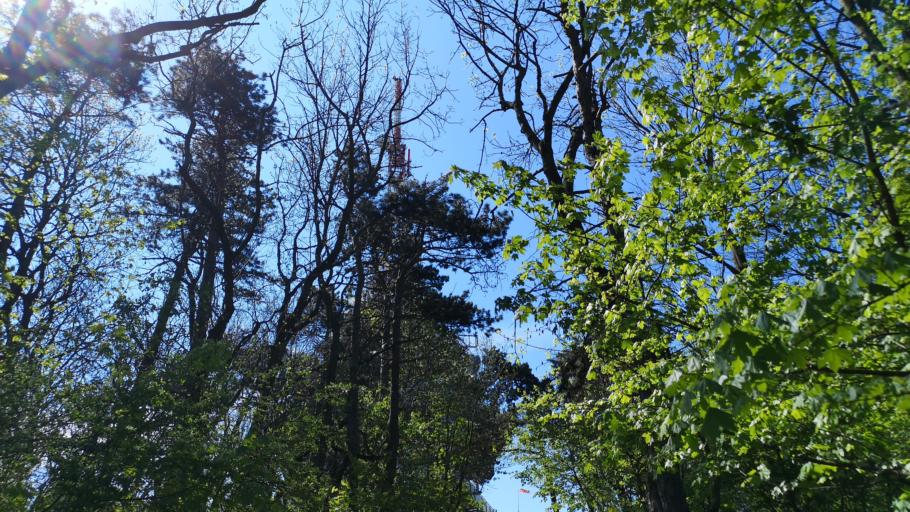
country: SK
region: Nitriansky
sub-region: Okres Nitra
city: Nitra
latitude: 48.3437
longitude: 18.1053
